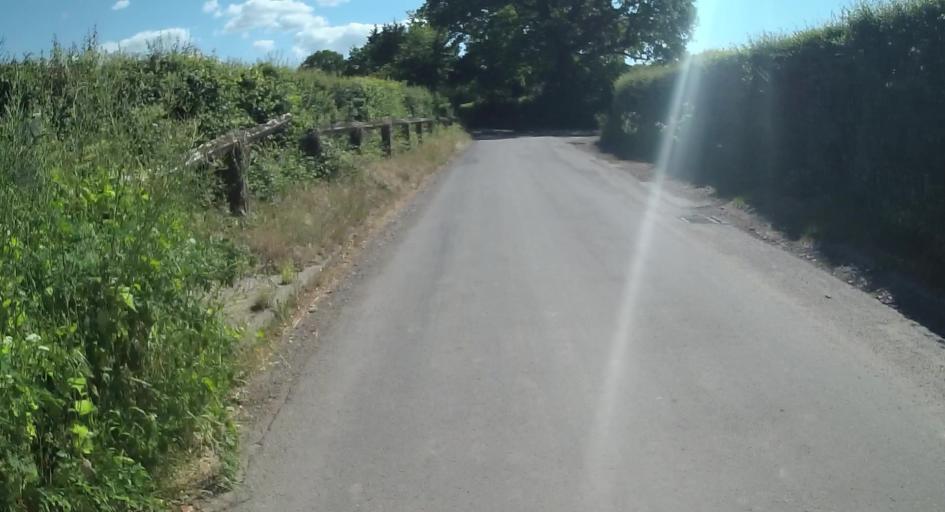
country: GB
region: England
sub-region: Hampshire
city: Old Basing
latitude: 51.2724
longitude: -0.9992
